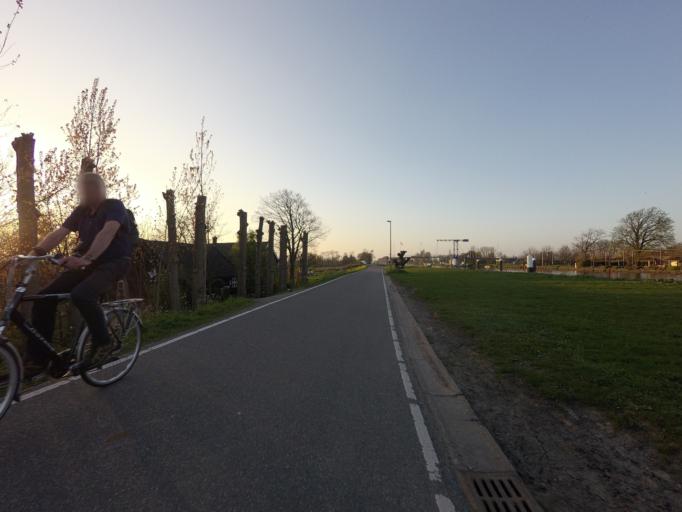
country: NL
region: South Holland
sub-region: Gemeente Schiedam
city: Schiedam
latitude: 51.9624
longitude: 4.3931
